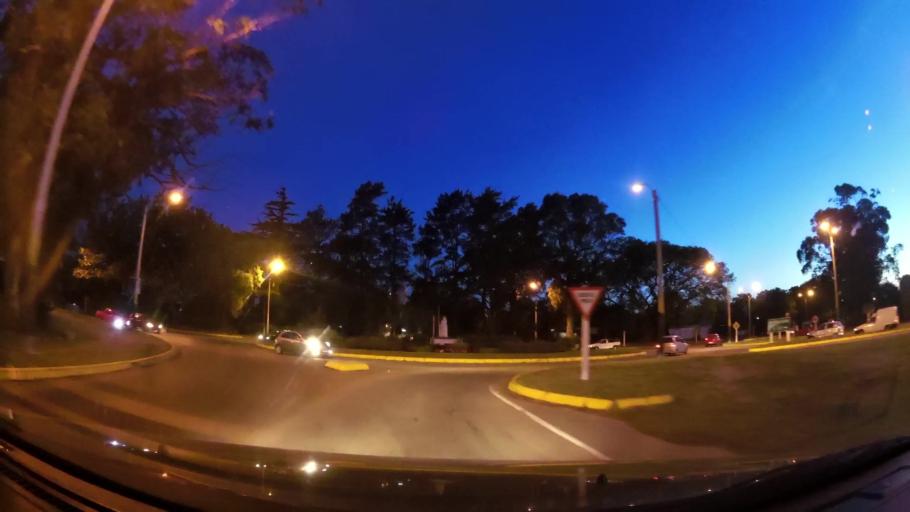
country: UY
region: Canelones
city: Atlantida
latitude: -34.7691
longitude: -55.7636
